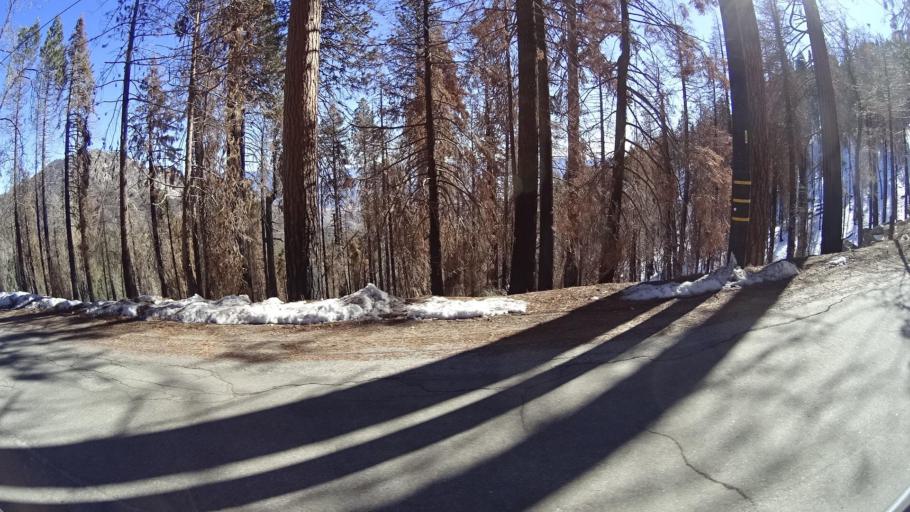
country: US
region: California
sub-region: Kern County
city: Alta Sierra
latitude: 35.7268
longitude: -118.5574
